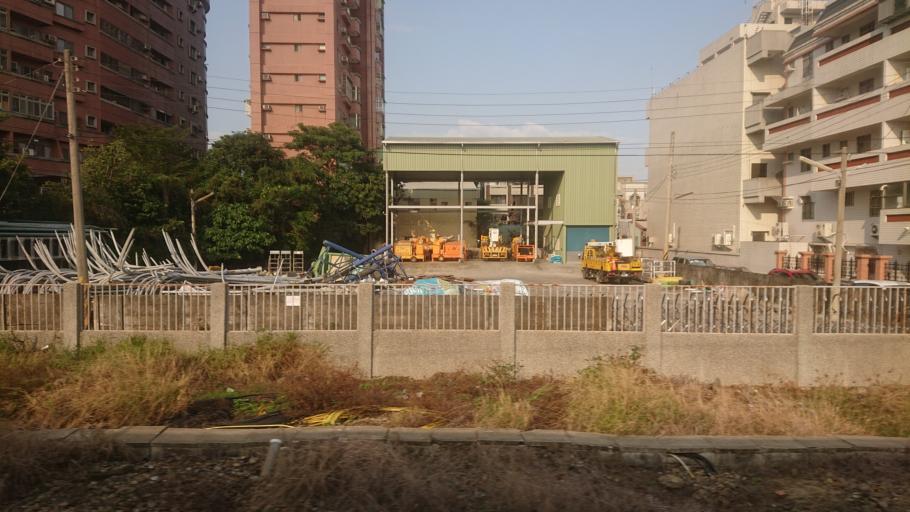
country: TW
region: Taiwan
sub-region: Chiayi
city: Jiayi Shi
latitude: 23.5530
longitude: 120.4310
